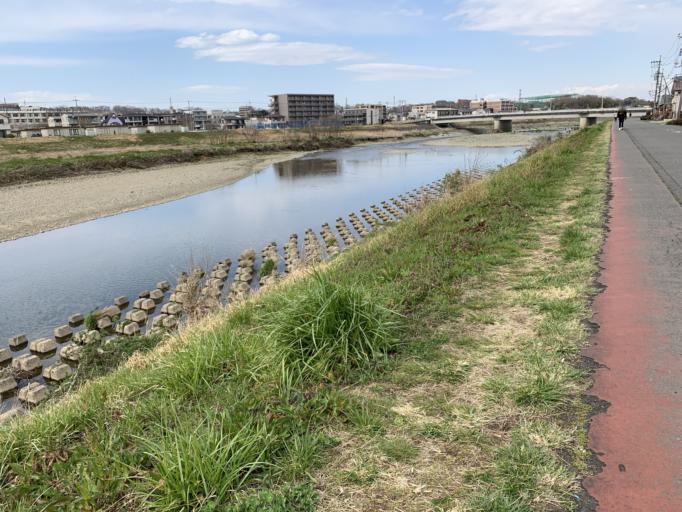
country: JP
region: Tokyo
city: Hino
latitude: 35.6577
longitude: 139.3919
